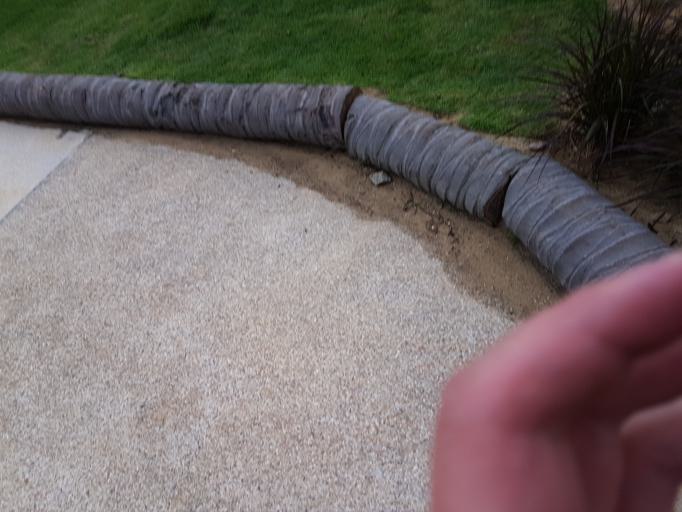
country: SG
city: Singapore
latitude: 1.2562
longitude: 103.8118
